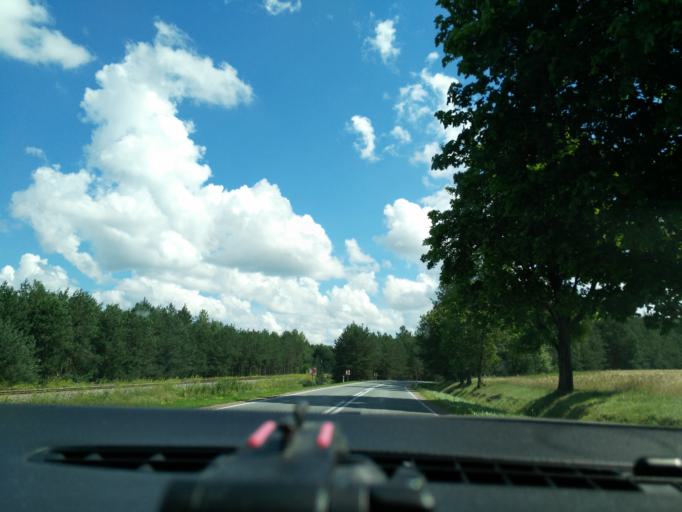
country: PL
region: Masovian Voivodeship
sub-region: Powiat losicki
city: Sarnaki
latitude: 52.3080
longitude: 22.8388
